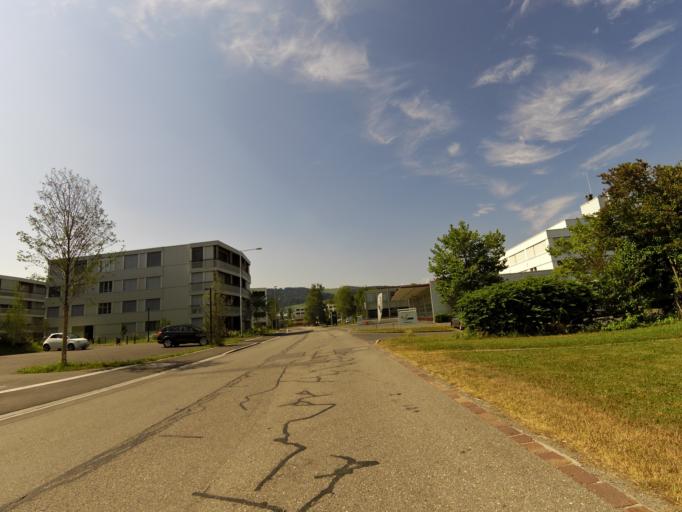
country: CH
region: Lucerne
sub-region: Lucerne-Land District
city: Meierskappel
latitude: 47.1461
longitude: 8.4348
